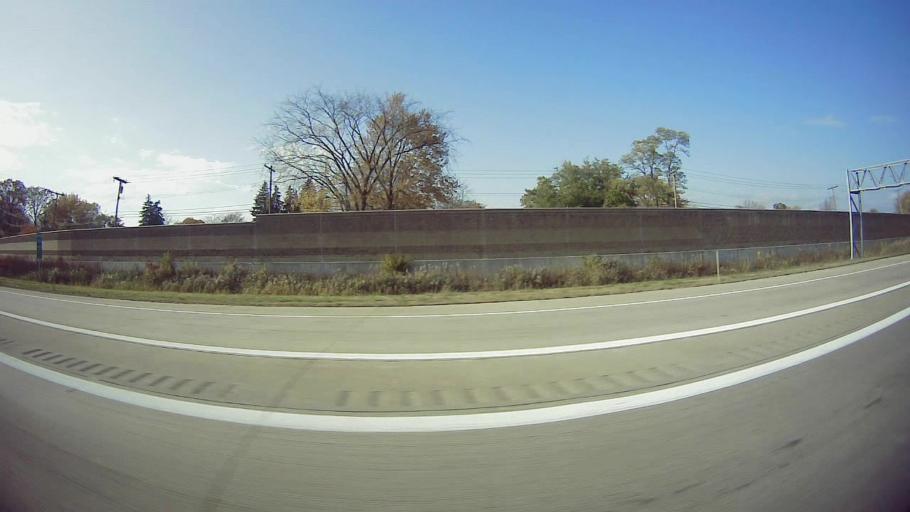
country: US
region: Michigan
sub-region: Wayne County
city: Rockwood
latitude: 42.0714
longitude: -83.2516
